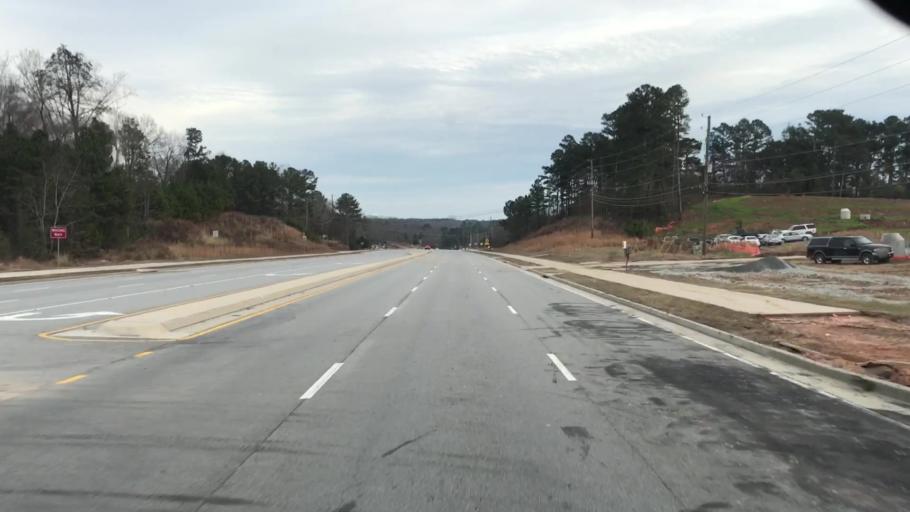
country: US
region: Georgia
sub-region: Hall County
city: Flowery Branch
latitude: 34.1154
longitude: -83.9036
